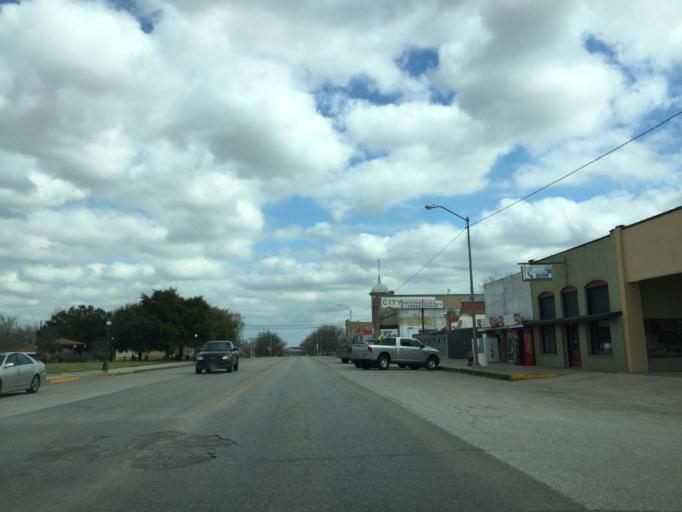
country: US
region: Texas
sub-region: Williamson County
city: Granger
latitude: 30.7176
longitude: -97.4419
